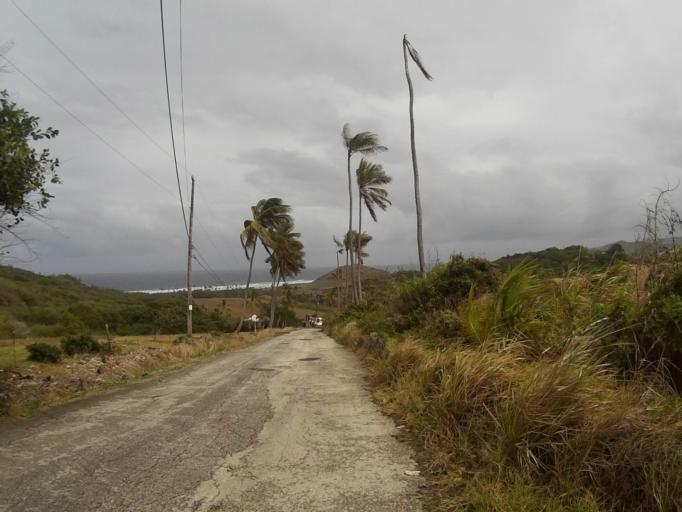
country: BB
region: Saint Andrew
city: Greenland
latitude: 13.2682
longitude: -59.5738
